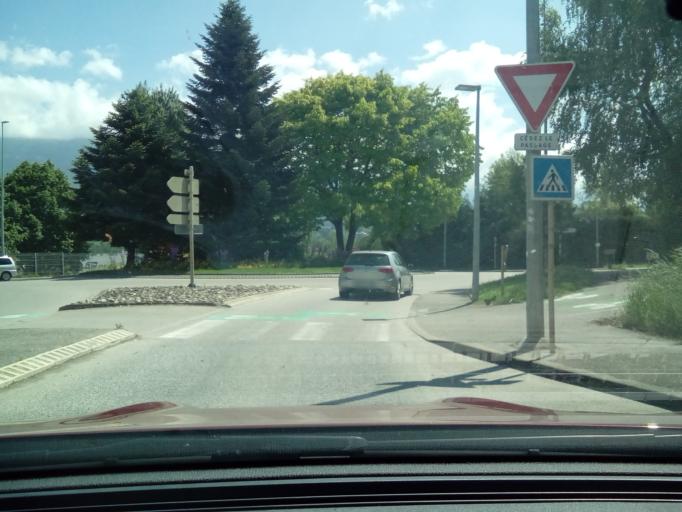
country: FR
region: Rhone-Alpes
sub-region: Departement de la Savoie
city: La Motte-Servolex
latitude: 45.6009
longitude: 5.8760
